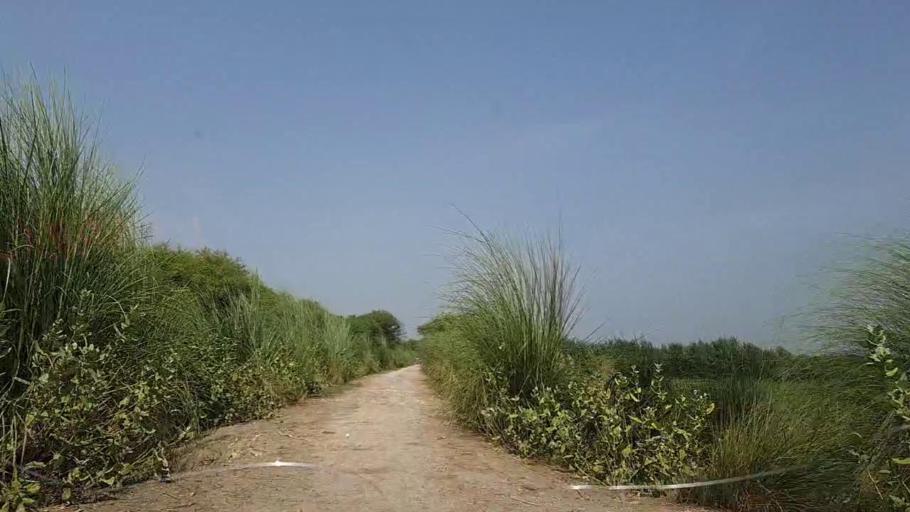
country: PK
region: Sindh
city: Ghotki
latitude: 28.0812
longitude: 69.3322
